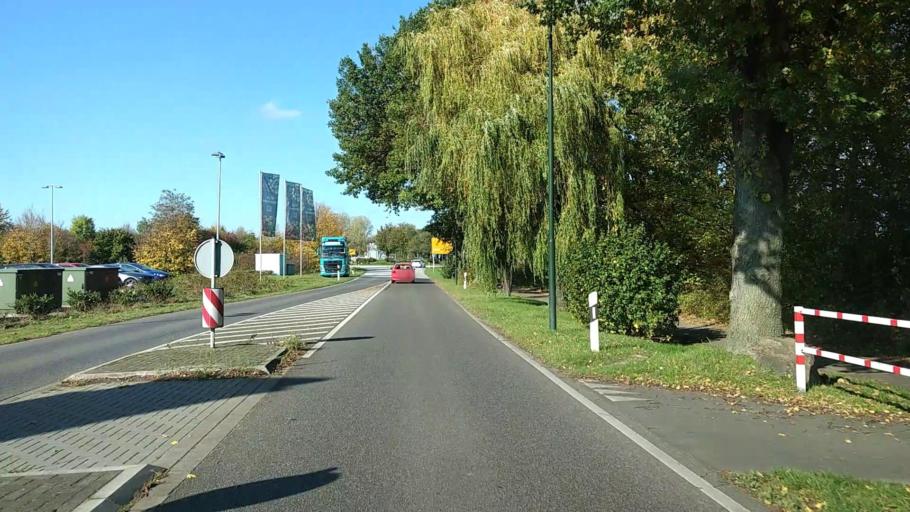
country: DE
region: North Rhine-Westphalia
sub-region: Regierungsbezirk Koln
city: Kerpen
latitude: 50.9129
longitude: 6.6689
